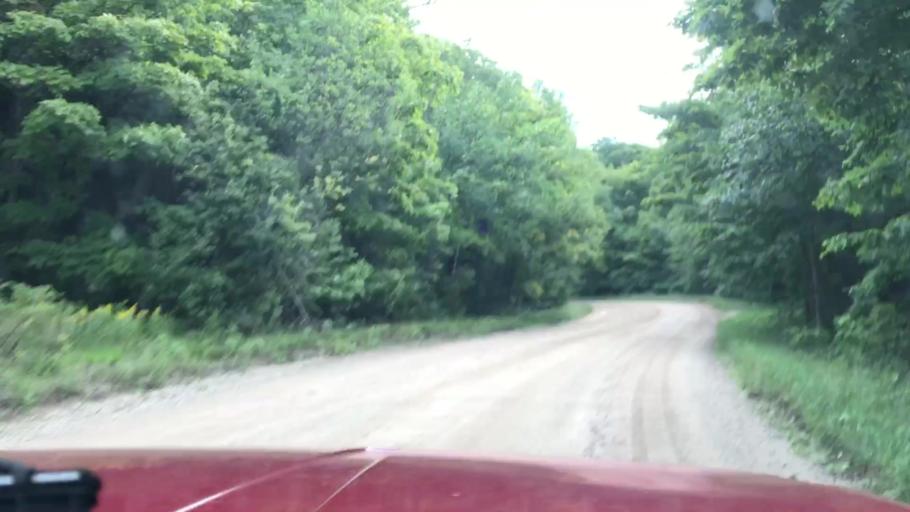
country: US
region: Michigan
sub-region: Charlevoix County
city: Charlevoix
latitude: 45.7329
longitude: -85.5618
